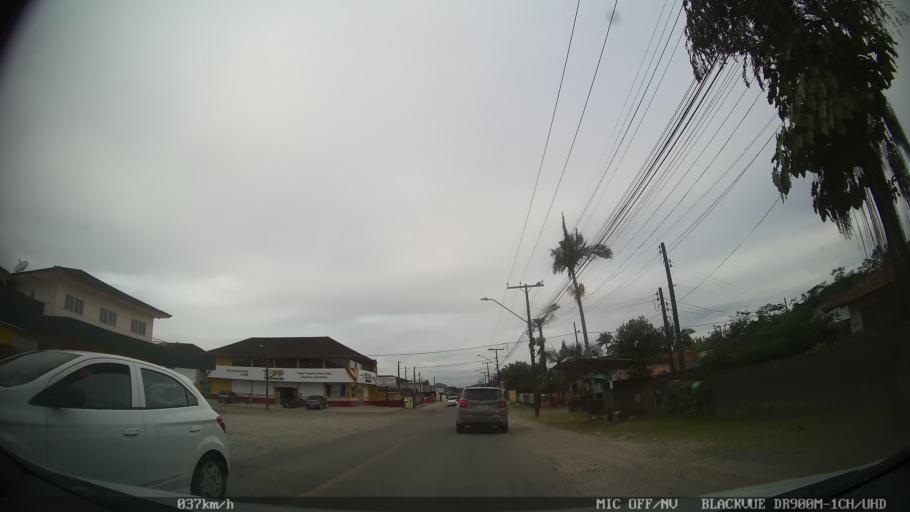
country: BR
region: Santa Catarina
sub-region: Joinville
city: Joinville
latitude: -26.3372
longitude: -48.9001
